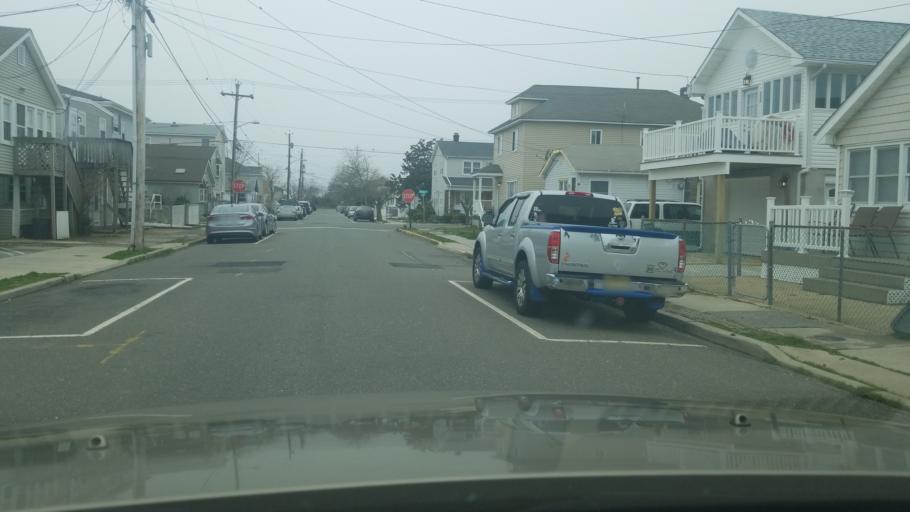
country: US
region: New Jersey
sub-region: Ocean County
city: Seaside Heights
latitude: 39.9396
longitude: -74.0771
